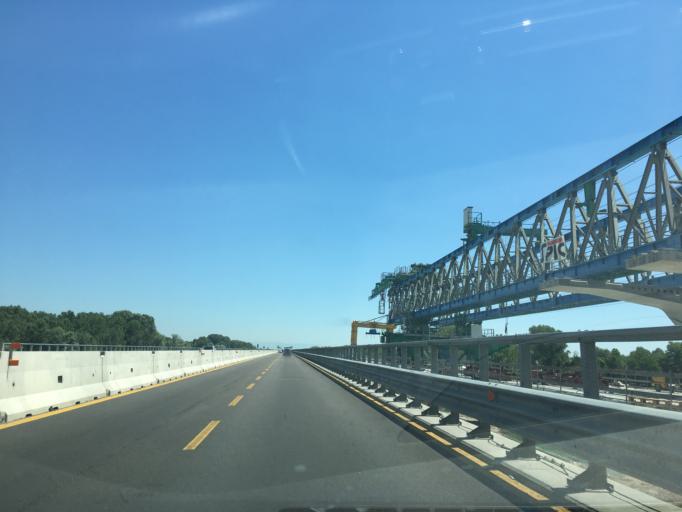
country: IT
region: Friuli Venezia Giulia
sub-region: Provincia di Udine
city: Ronchis
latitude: 45.8118
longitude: 12.9774
